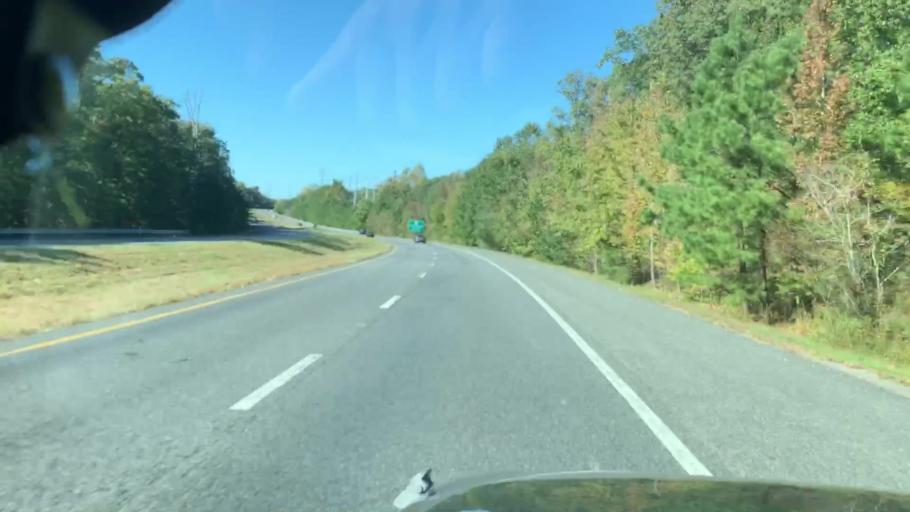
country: US
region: Virginia
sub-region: James City County
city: Williamsburg
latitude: 37.3191
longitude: -76.7498
